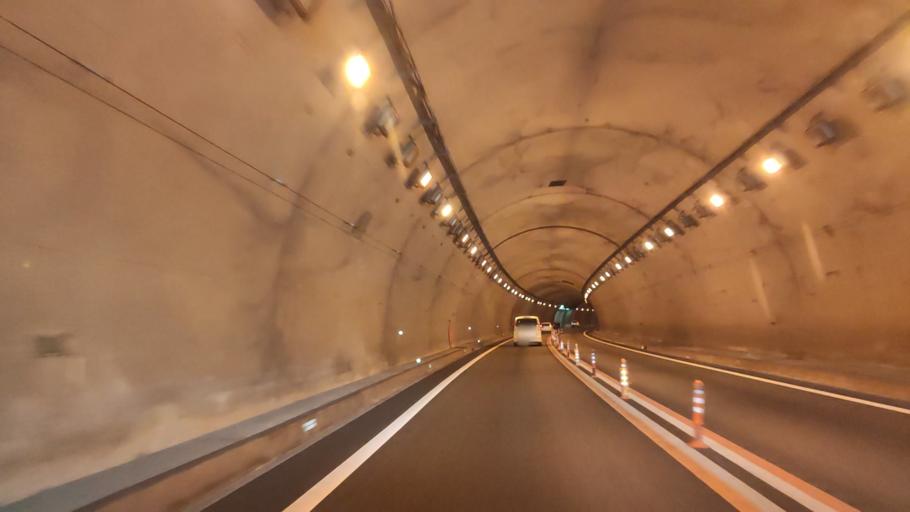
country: JP
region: Ehime
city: Kawanoecho
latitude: 33.9985
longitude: 133.6407
